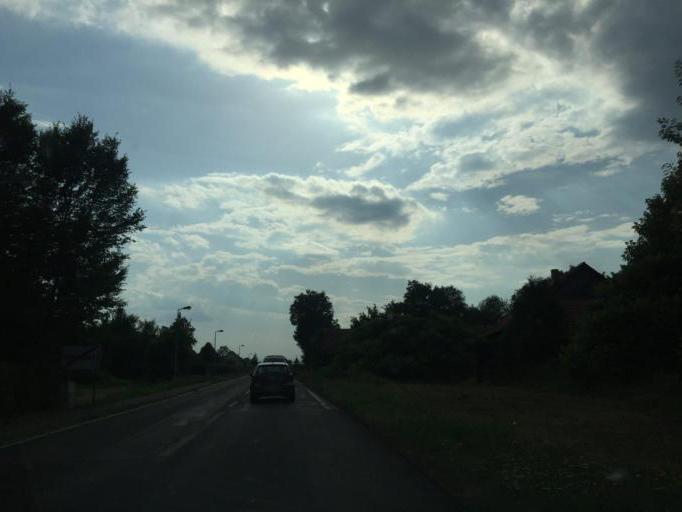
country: AT
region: Styria
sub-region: Politischer Bezirk Suedoststeiermark
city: Ratschendorf
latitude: 46.7289
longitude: 15.8326
